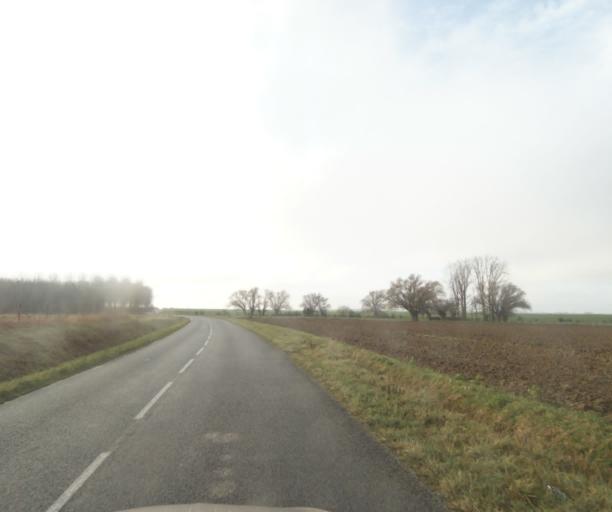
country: FR
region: Nord-Pas-de-Calais
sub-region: Departement du Nord
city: Haspres
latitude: 50.2741
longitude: 3.4336
